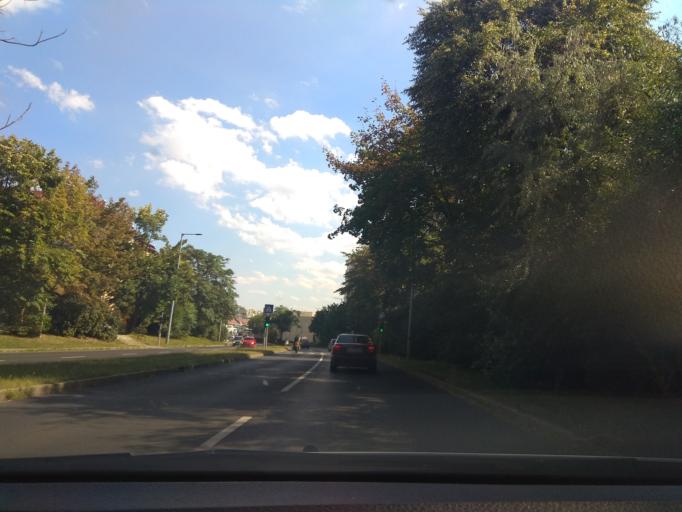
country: HU
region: Borsod-Abauj-Zemplen
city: Miskolc
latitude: 48.1086
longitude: 20.7883
